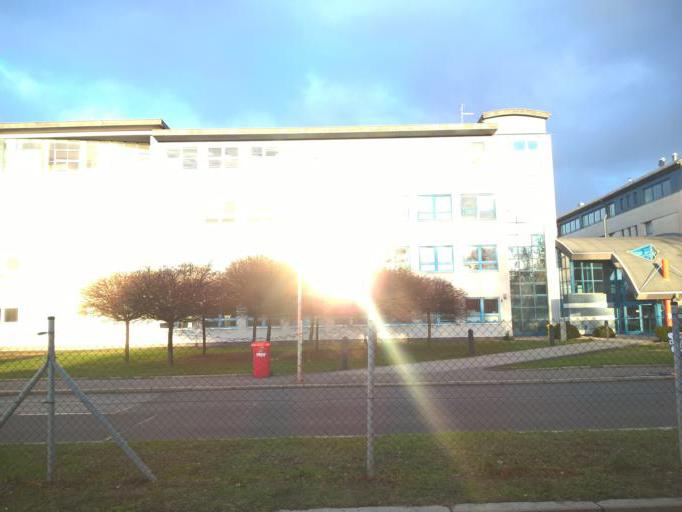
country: CZ
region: Central Bohemia
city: Hostivice
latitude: 50.0980
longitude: 14.2900
